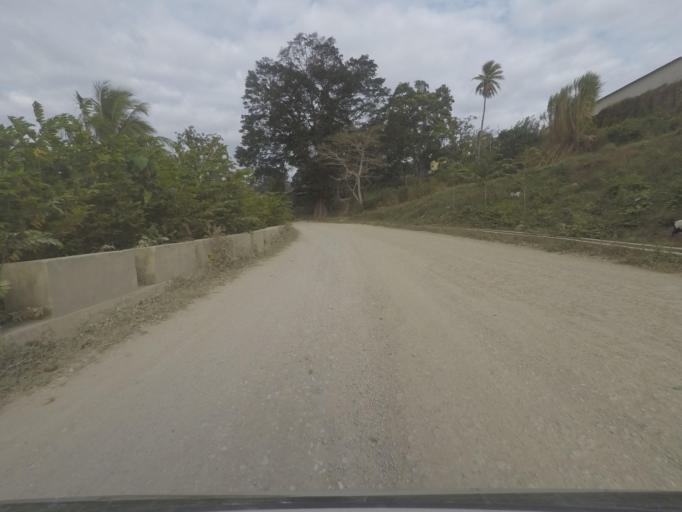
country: TL
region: Baucau
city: Venilale
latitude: -8.5919
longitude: 126.3871
